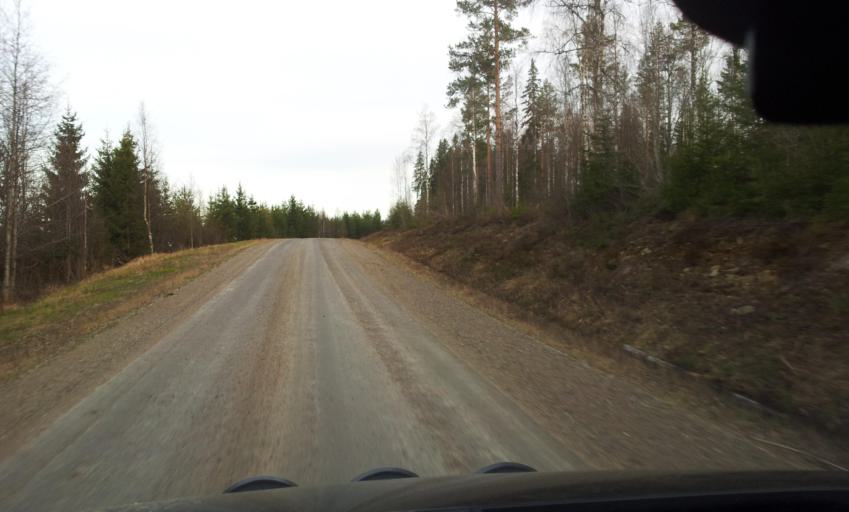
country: SE
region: Gaevleborg
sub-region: Ljusdals Kommun
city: Farila
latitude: 62.0855
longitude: 15.7687
